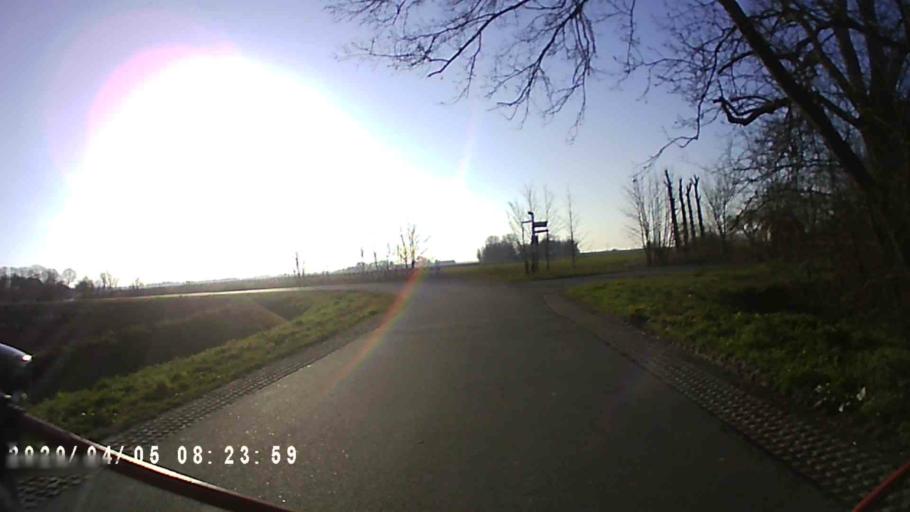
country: NL
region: Groningen
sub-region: Gemeente Winsum
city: Winsum
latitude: 53.3297
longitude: 6.4640
